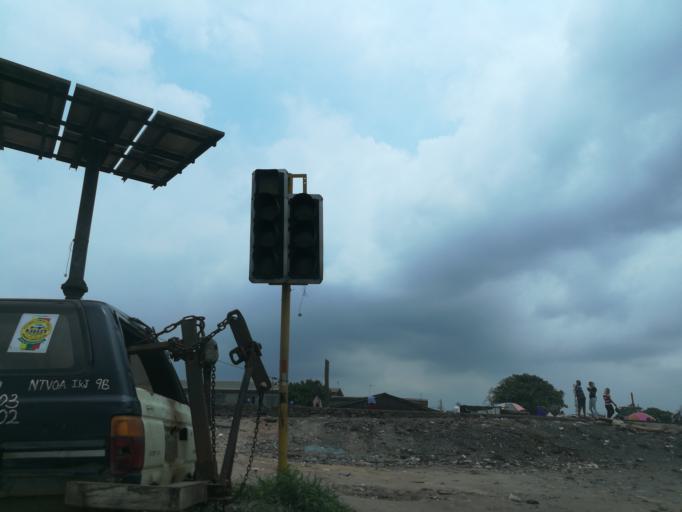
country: NG
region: Lagos
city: Agege
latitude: 6.6141
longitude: 3.3281
